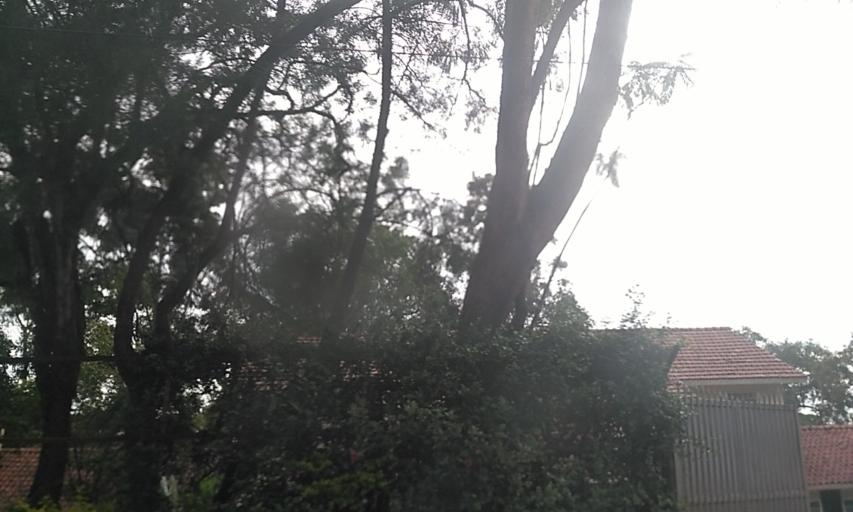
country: UG
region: Central Region
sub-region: Kampala District
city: Kampala
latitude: 0.3302
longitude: 32.5965
